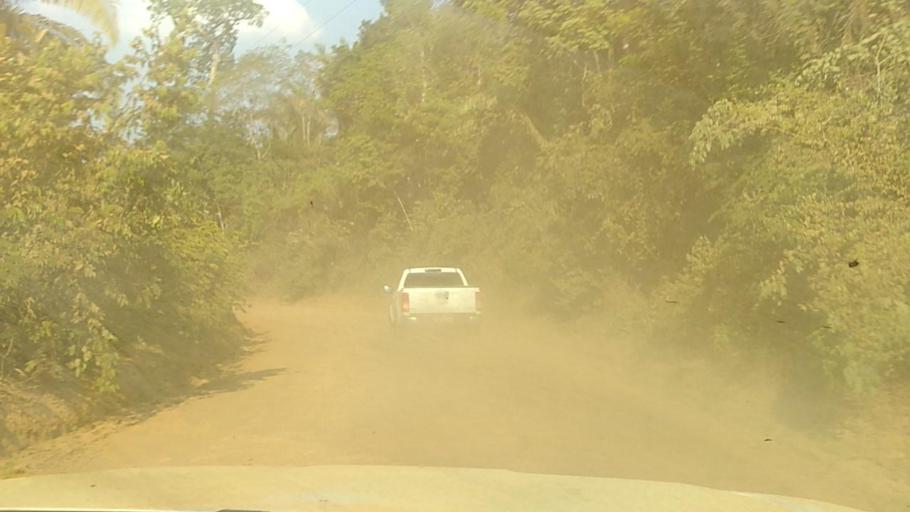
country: BR
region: Rondonia
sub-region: Porto Velho
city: Porto Velho
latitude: -8.6712
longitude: -64.0014
